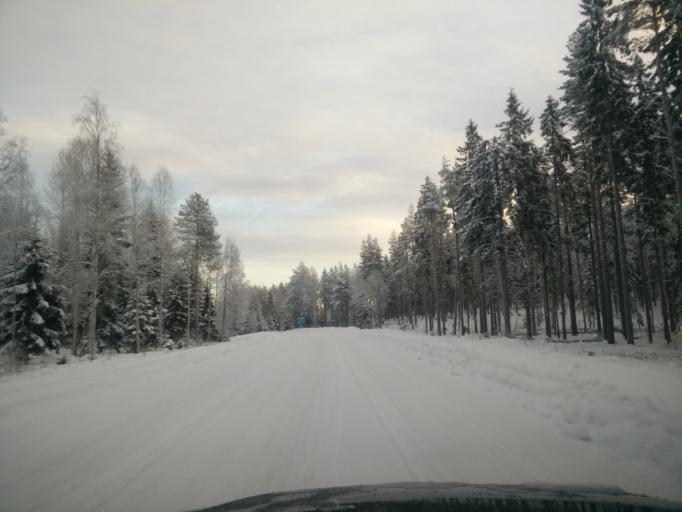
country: SE
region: Vaesternorrland
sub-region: Sundsvalls Kommun
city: Njurundabommen
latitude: 62.2147
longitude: 17.3692
